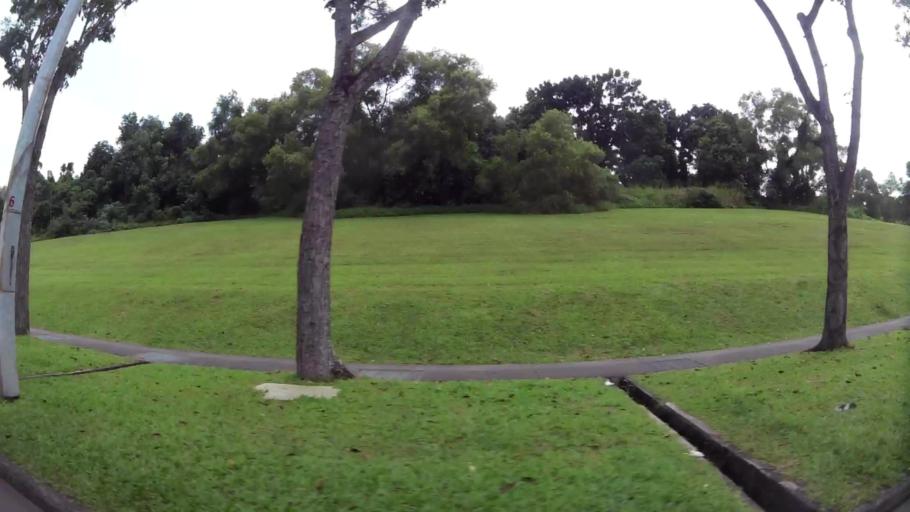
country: SG
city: Singapore
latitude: 1.3427
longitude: 103.9377
